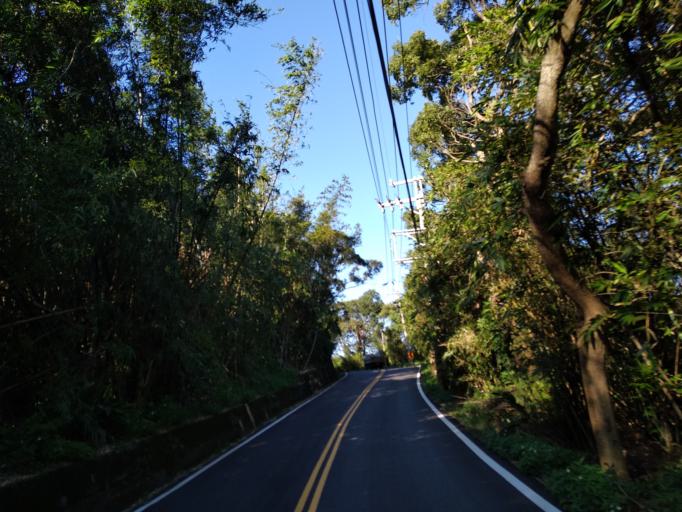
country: TW
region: Taiwan
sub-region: Hsinchu
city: Zhubei
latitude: 24.8590
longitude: 121.0954
